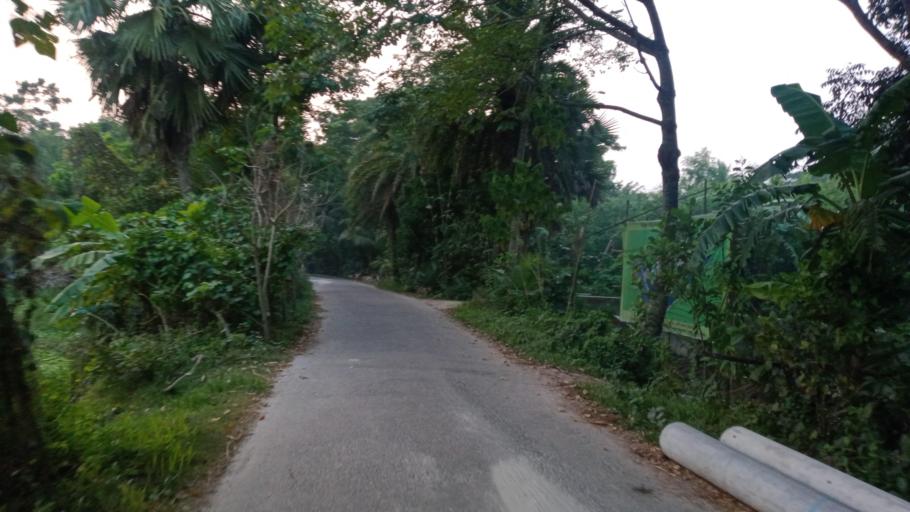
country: BD
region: Chittagong
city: Hajiganj
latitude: 23.3675
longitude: 90.9849
